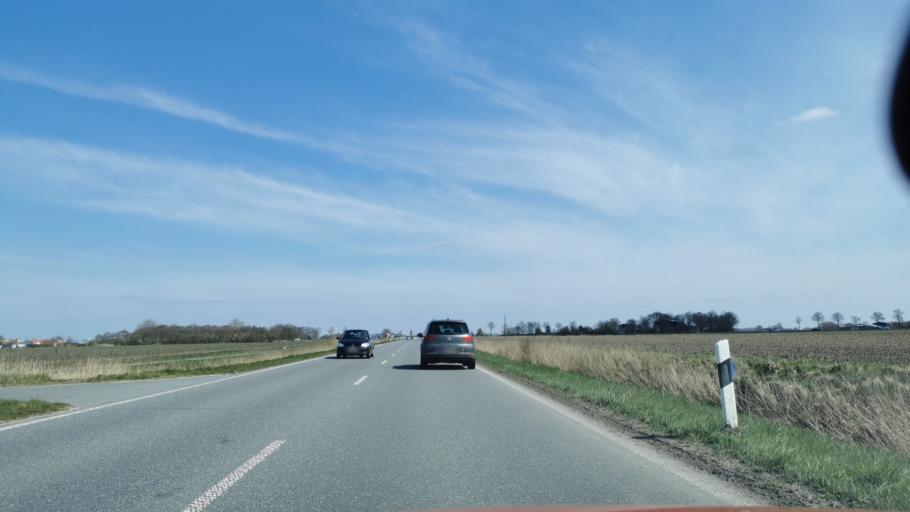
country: DE
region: Schleswig-Holstein
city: Oesterdeichstrich
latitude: 54.1449
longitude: 8.8696
